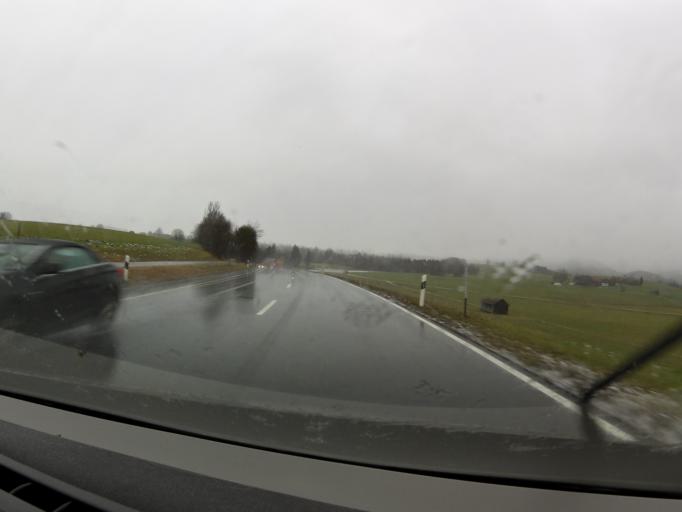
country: DE
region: Bavaria
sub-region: Upper Bavaria
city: Gaissach
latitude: 47.7596
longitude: 11.5911
